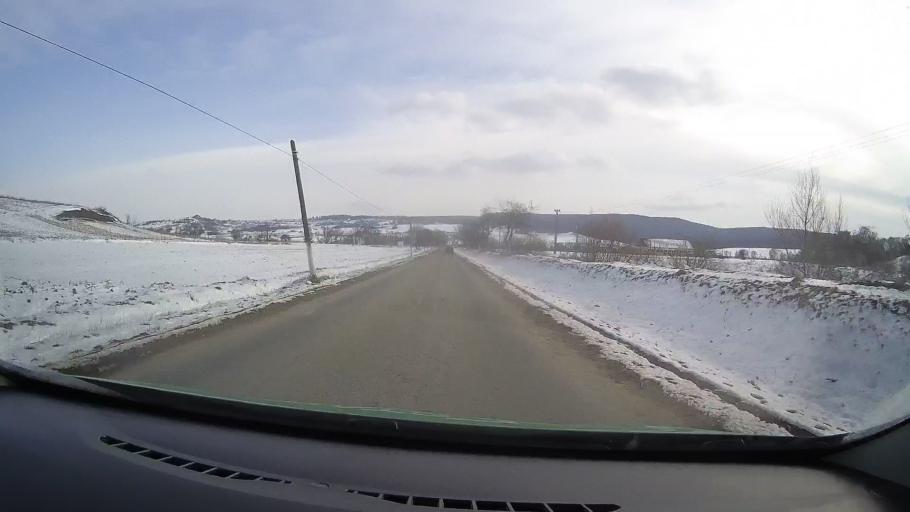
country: RO
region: Sibiu
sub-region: Comuna Iacobeni
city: Iacobeni
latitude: 46.0422
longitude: 24.7294
